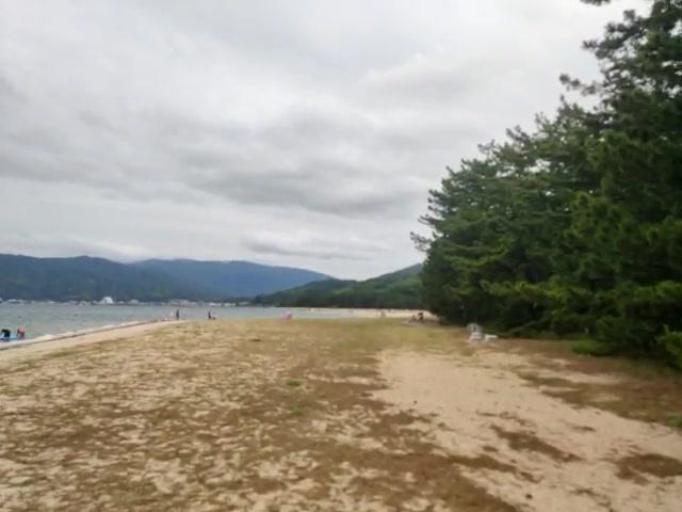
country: JP
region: Kyoto
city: Miyazu
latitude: 35.5613
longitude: 135.1879
